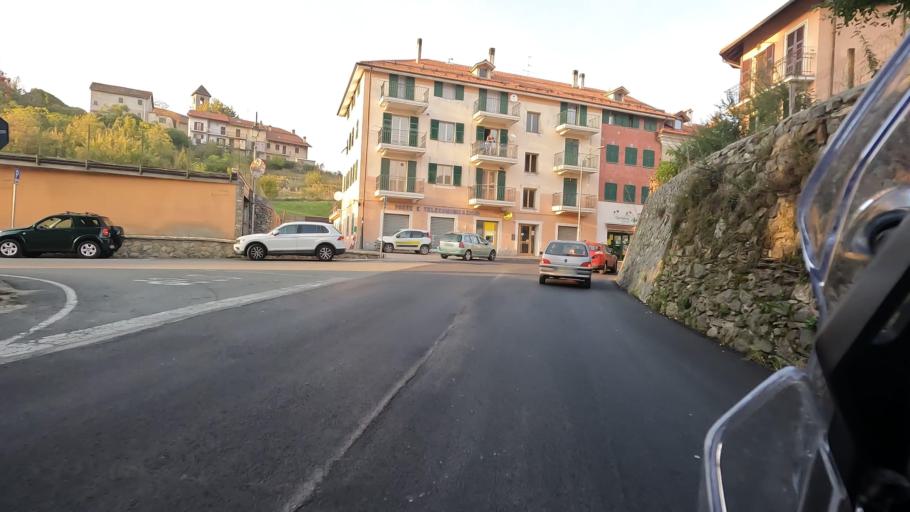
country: IT
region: Liguria
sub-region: Provincia di Savona
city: Sassello
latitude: 44.4788
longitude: 8.4889
